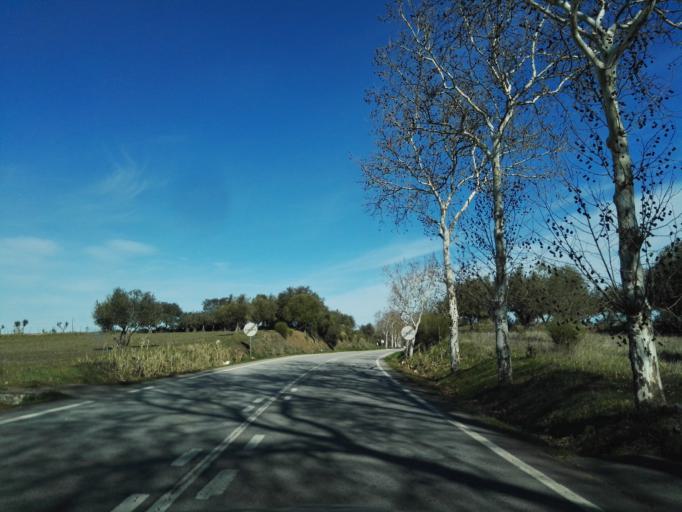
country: PT
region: Portalegre
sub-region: Arronches
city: Arronches
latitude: 39.1280
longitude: -7.2952
